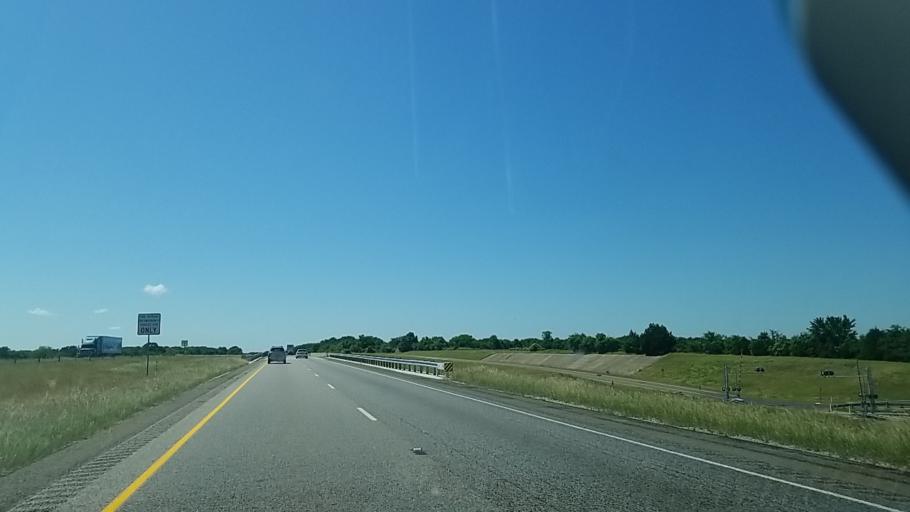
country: US
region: Texas
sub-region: Freestone County
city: Fairfield
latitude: 31.7708
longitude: -96.2207
